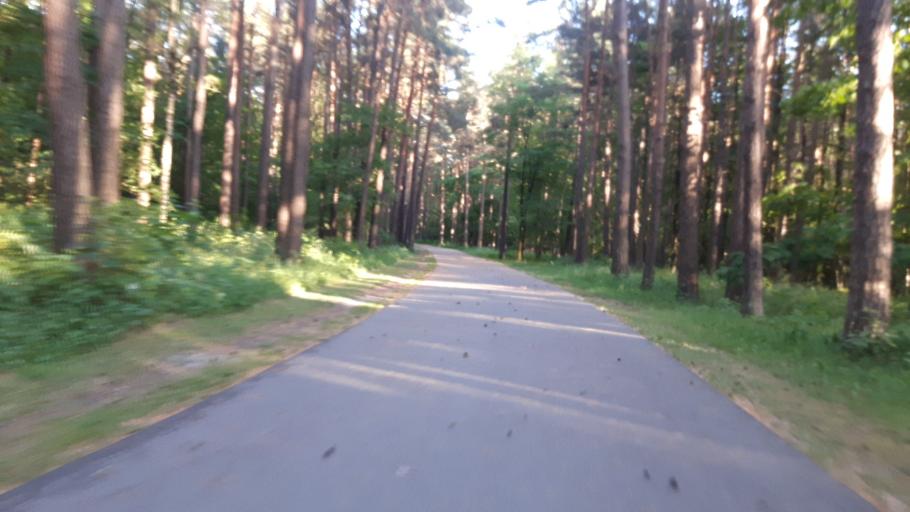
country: LV
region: Riga
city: Jaunciems
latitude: 57.0024
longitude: 24.1449
